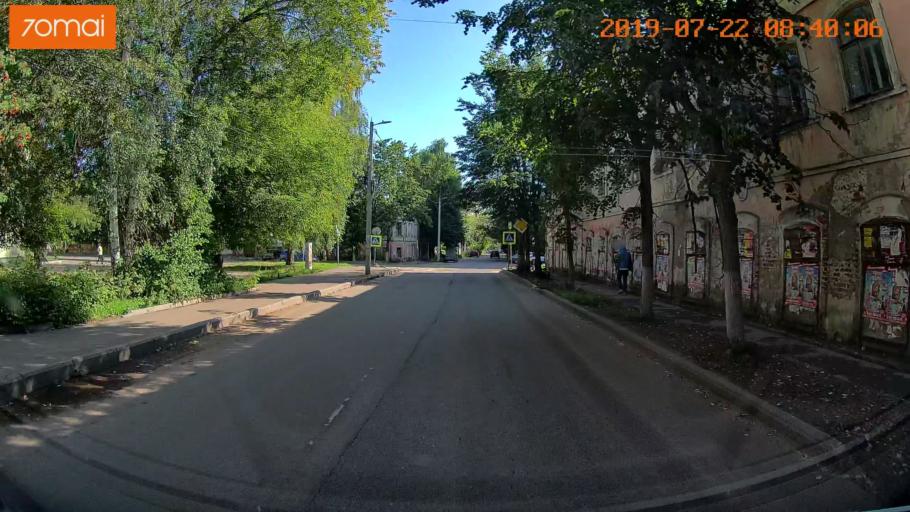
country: RU
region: Ivanovo
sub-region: Gorod Ivanovo
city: Ivanovo
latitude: 56.9963
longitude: 40.9890
